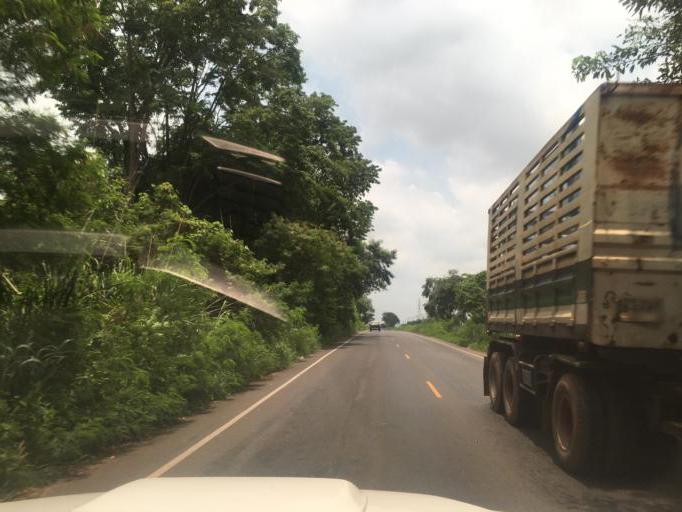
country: TH
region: Changwat Udon Thani
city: Udon Thani
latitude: 17.3099
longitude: 102.7087
